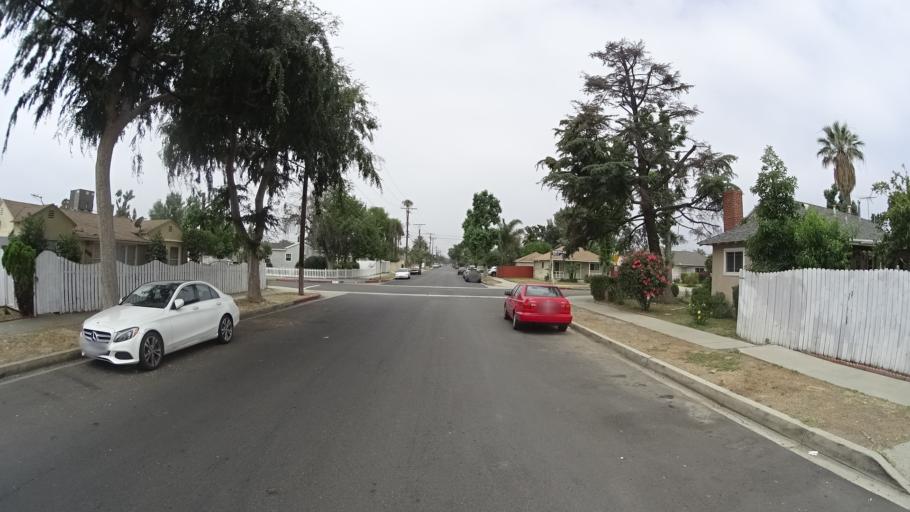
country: US
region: California
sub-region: Los Angeles County
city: North Hollywood
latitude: 34.1903
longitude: -118.4060
